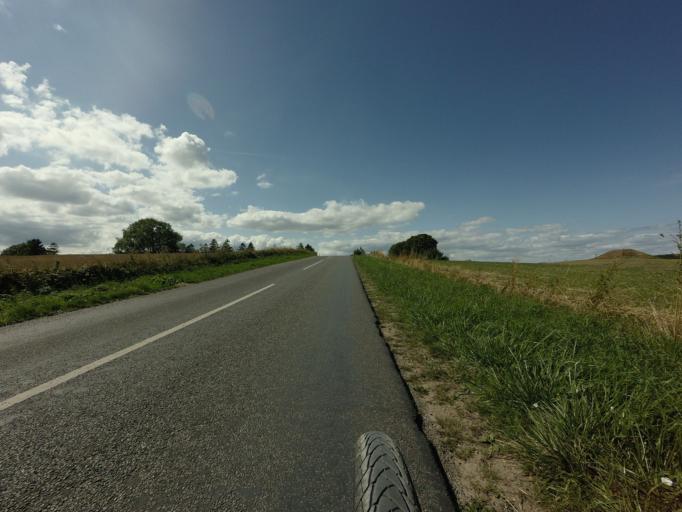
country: DK
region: Zealand
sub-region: Vordingborg Kommune
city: Stege
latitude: 54.9999
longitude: 12.5139
